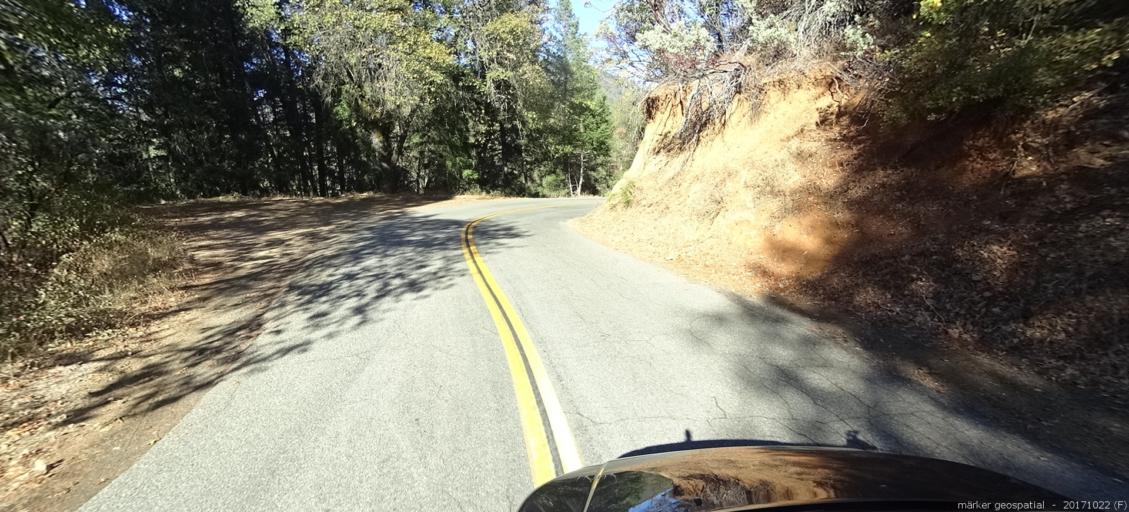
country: US
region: California
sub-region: Shasta County
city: Shasta Lake
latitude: 40.8462
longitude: -122.3463
